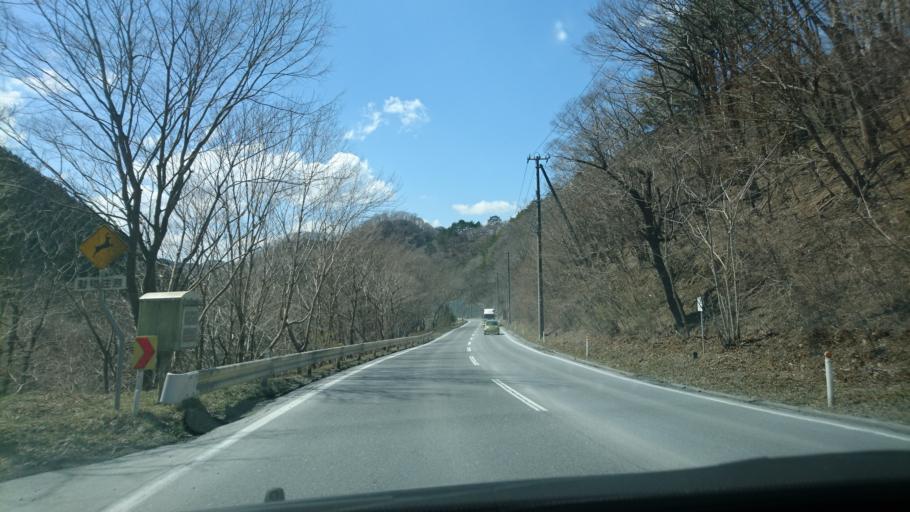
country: JP
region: Iwate
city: Ofunato
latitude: 39.1522
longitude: 141.6256
